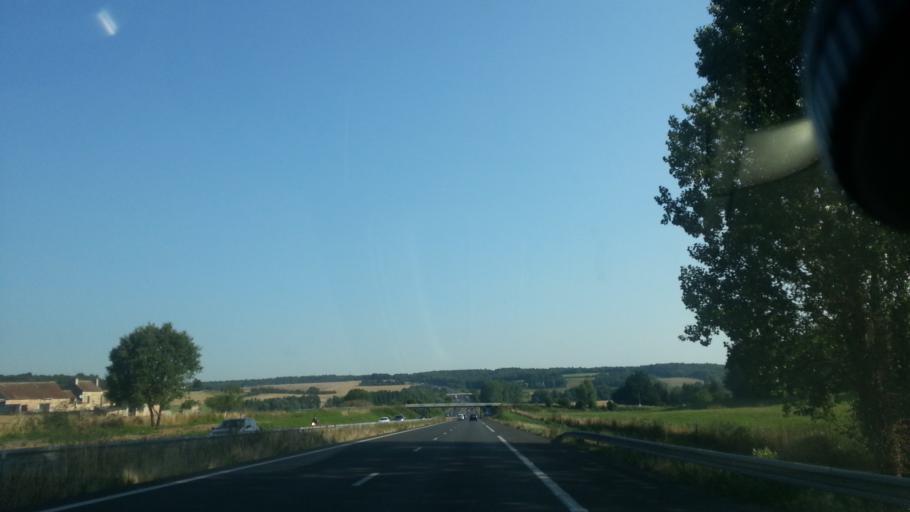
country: FR
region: Poitou-Charentes
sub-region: Departement de la Vienne
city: Dange-Saint-Romain
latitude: 46.9400
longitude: 0.5457
